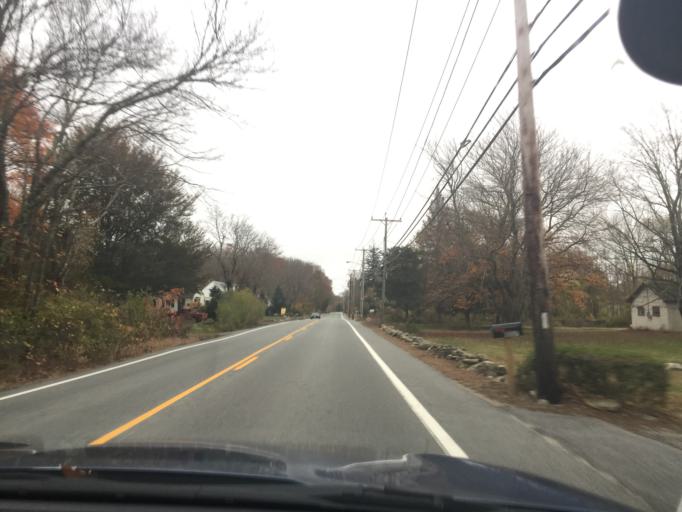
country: US
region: Rhode Island
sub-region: Providence County
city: Chepachet
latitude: 41.8386
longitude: -71.6763
